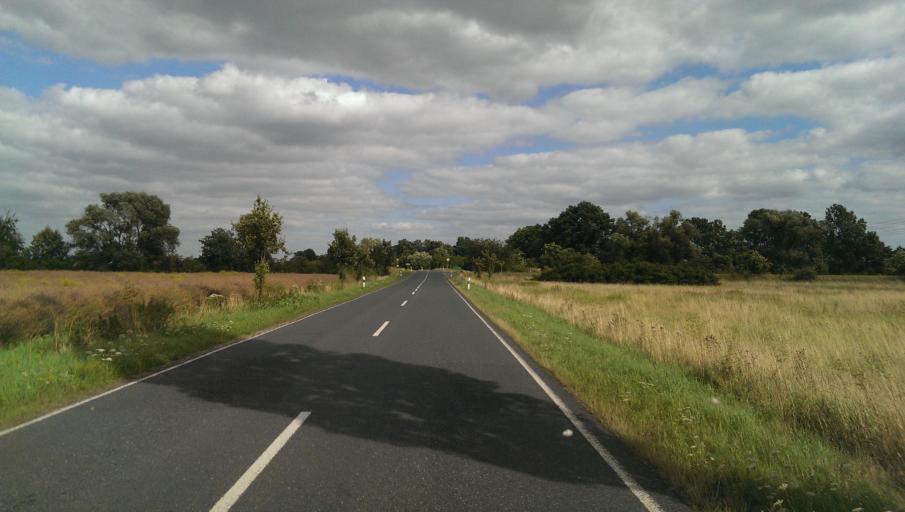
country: DE
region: Saxony-Anhalt
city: Worlitz
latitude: 51.8339
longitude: 12.4026
